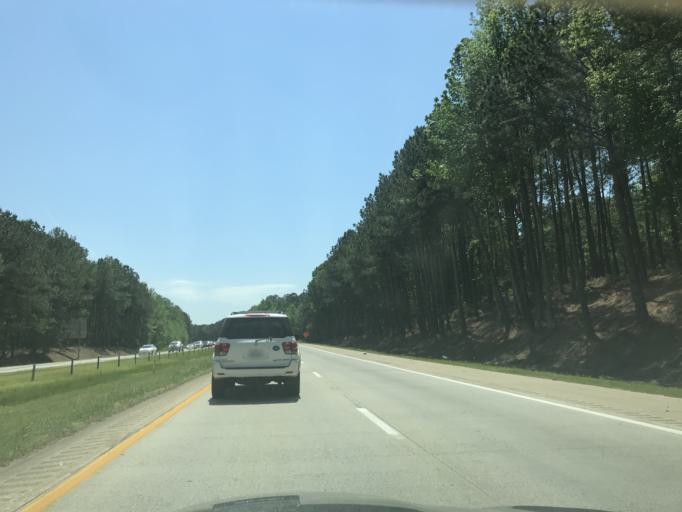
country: US
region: North Carolina
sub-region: Wake County
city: Garner
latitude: 35.5882
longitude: -78.5729
